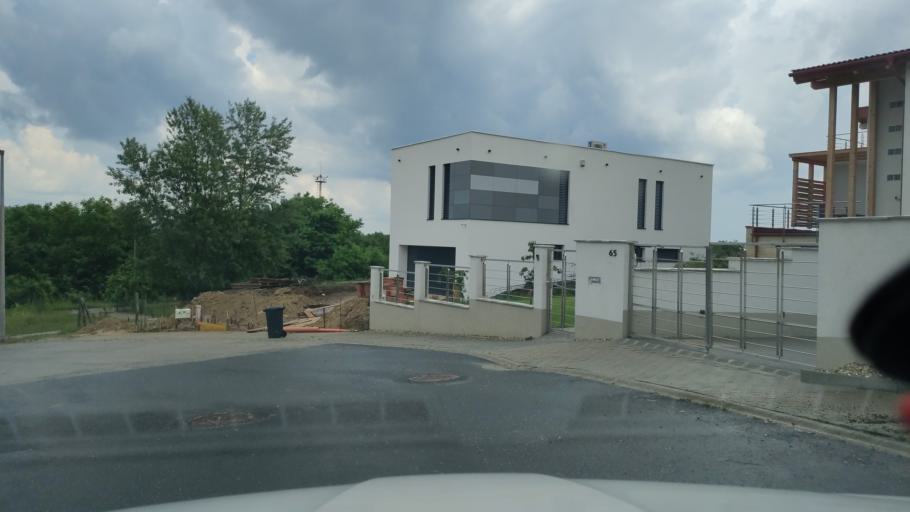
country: HU
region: Pest
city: Toeroekbalint
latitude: 47.4456
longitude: 18.9229
